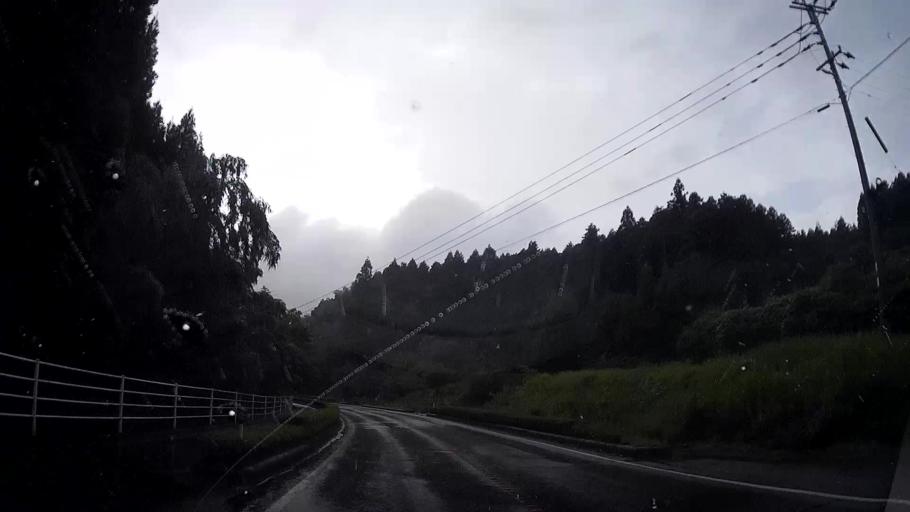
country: JP
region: Kumamoto
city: Aso
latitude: 32.8563
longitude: 131.0142
